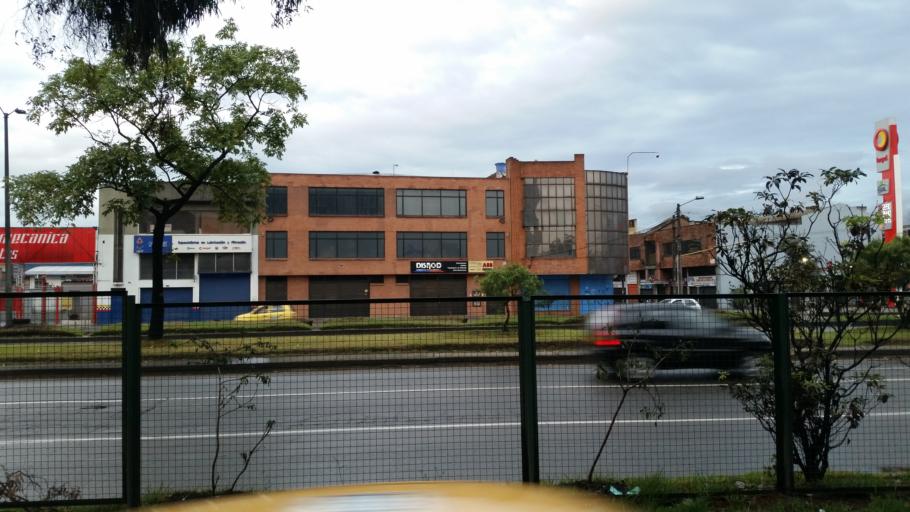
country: CO
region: Bogota D.C.
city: Bogota
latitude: 4.6304
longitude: -74.1106
